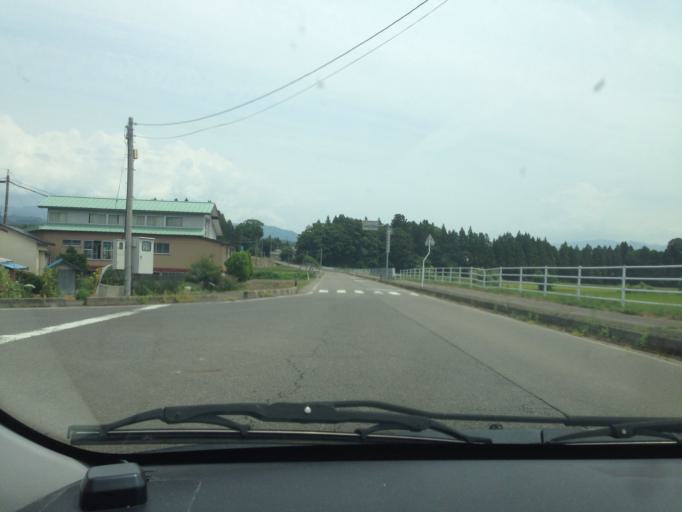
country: JP
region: Fukushima
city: Kitakata
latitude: 37.7090
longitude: 139.8501
